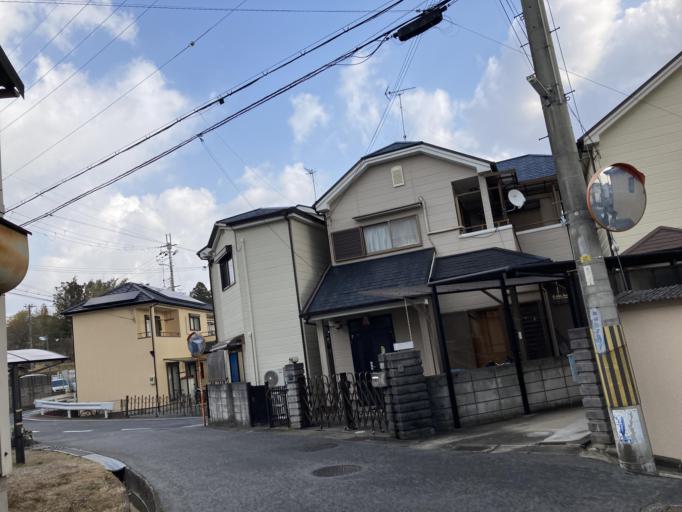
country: JP
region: Nara
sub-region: Ikoma-shi
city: Ikoma
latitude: 34.6088
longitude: 135.7220
